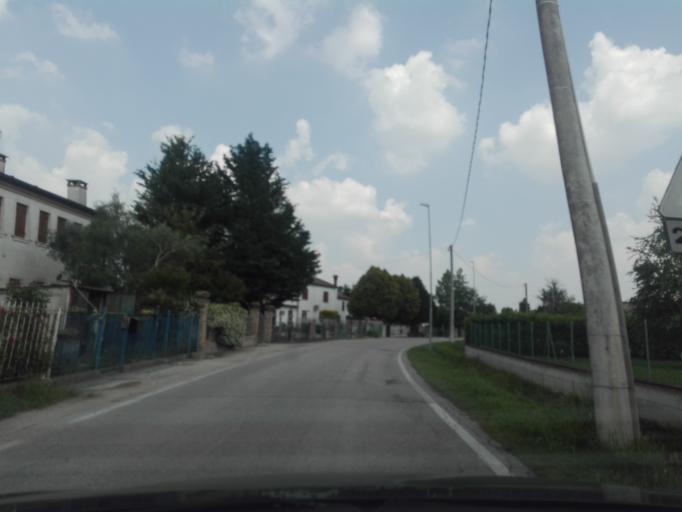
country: IT
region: Veneto
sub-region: Provincia di Rovigo
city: Crespino
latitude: 44.9923
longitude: 11.8962
